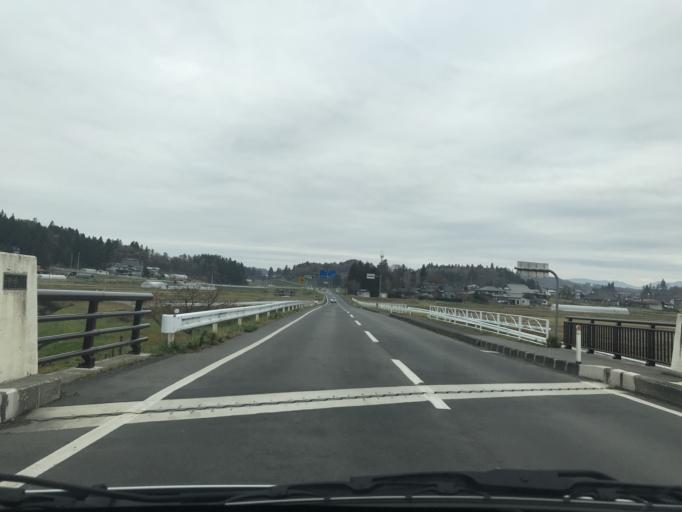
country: JP
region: Iwate
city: Mizusawa
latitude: 39.1874
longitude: 141.2220
